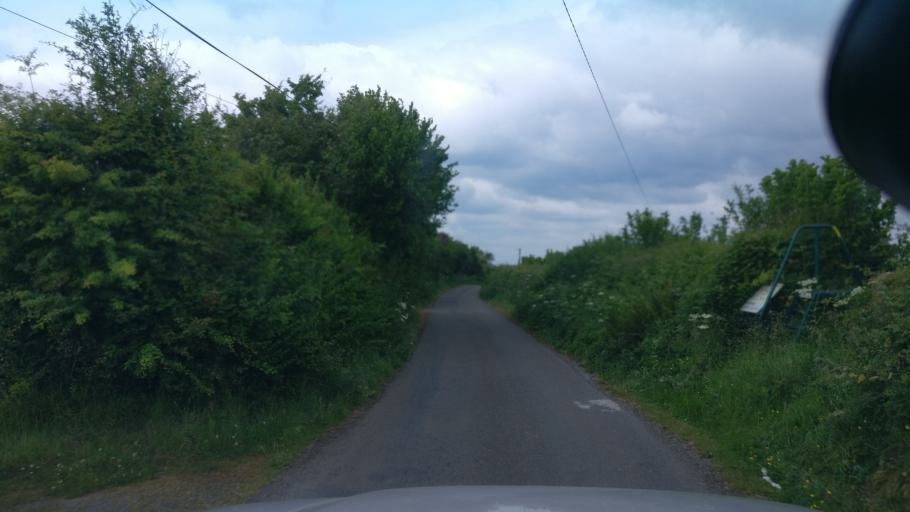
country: IE
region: Connaught
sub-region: County Galway
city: Ballinasloe
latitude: 53.2936
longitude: -8.3179
